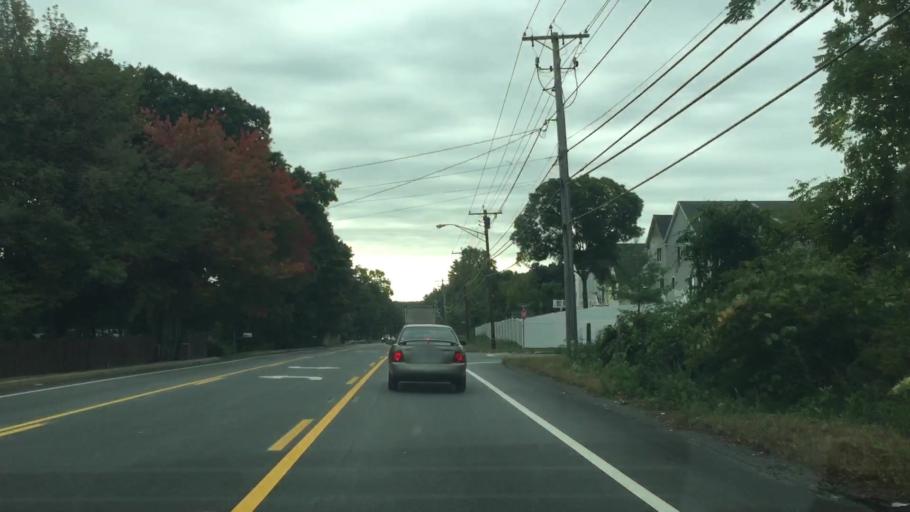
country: US
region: Massachusetts
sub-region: Essex County
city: Andover
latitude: 42.6558
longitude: -71.1020
